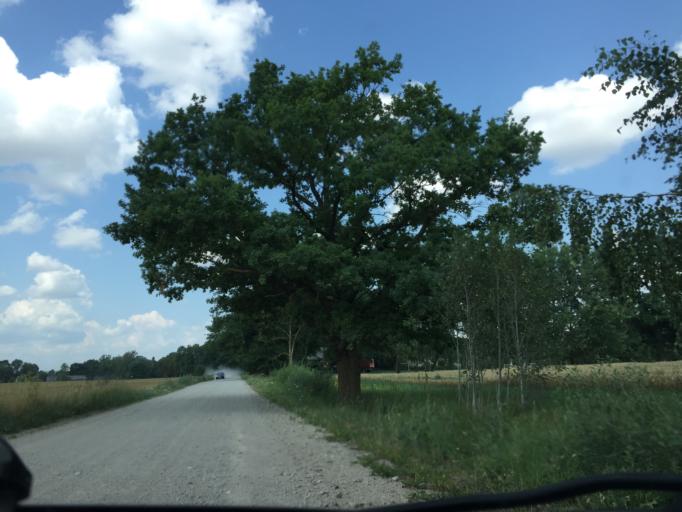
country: LT
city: Zagare
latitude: 56.3934
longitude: 23.2538
